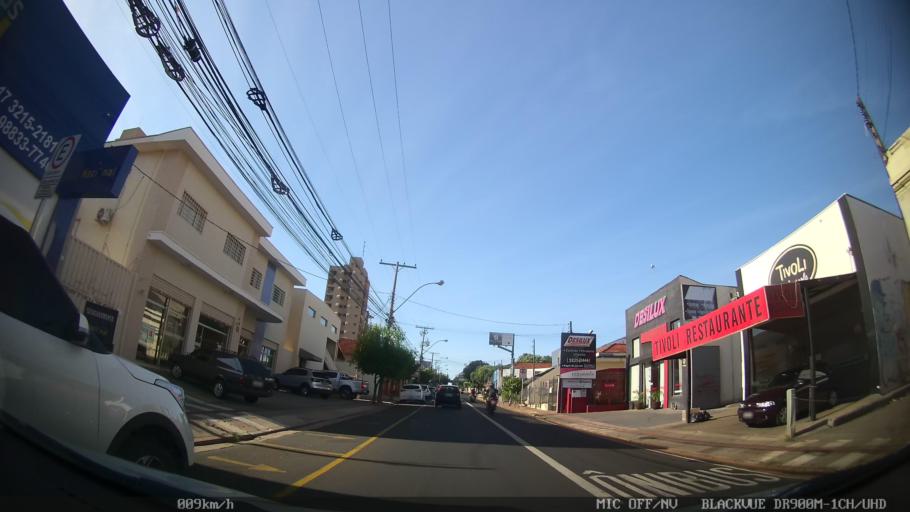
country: BR
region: Sao Paulo
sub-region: Sao Jose Do Rio Preto
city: Sao Jose do Rio Preto
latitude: -20.8044
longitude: -49.3734
